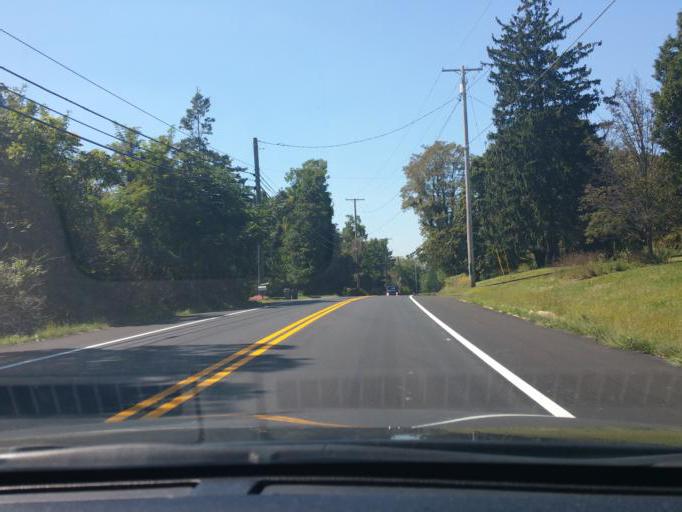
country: US
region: Maryland
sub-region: Harford County
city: Aberdeen
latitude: 39.5745
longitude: -76.2128
